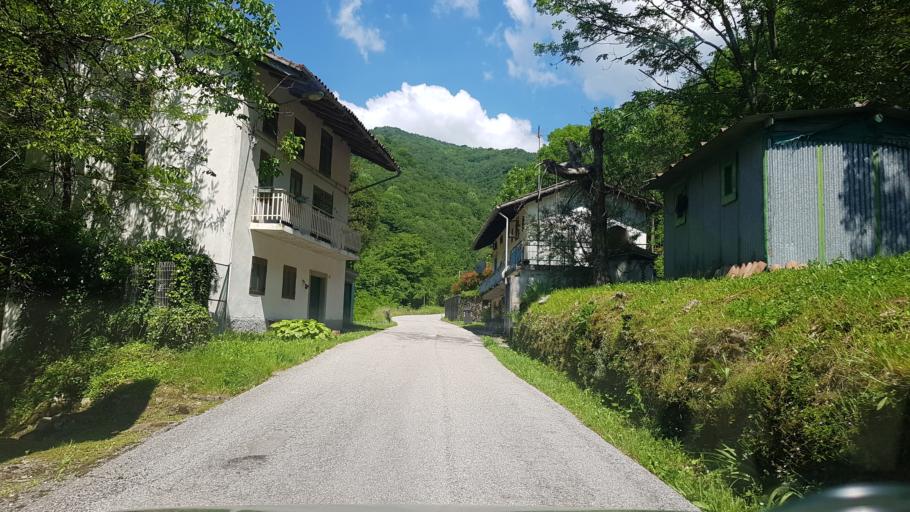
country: IT
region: Friuli Venezia Giulia
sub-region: Provincia di Udine
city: Torreano
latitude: 46.1550
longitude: 13.4334
